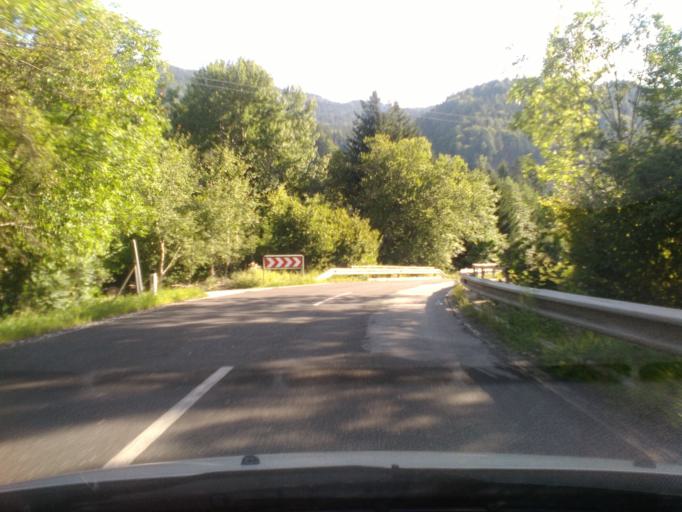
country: AT
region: Carinthia
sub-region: Politischer Bezirk Villach Land
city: Arnoldstein
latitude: 46.5425
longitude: 13.7753
